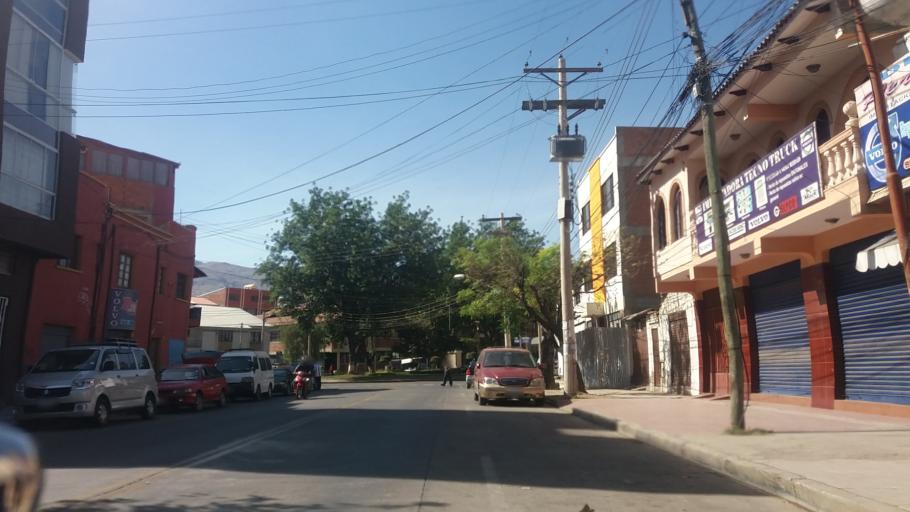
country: BO
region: Cochabamba
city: Cochabamba
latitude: -17.3979
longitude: -66.1632
